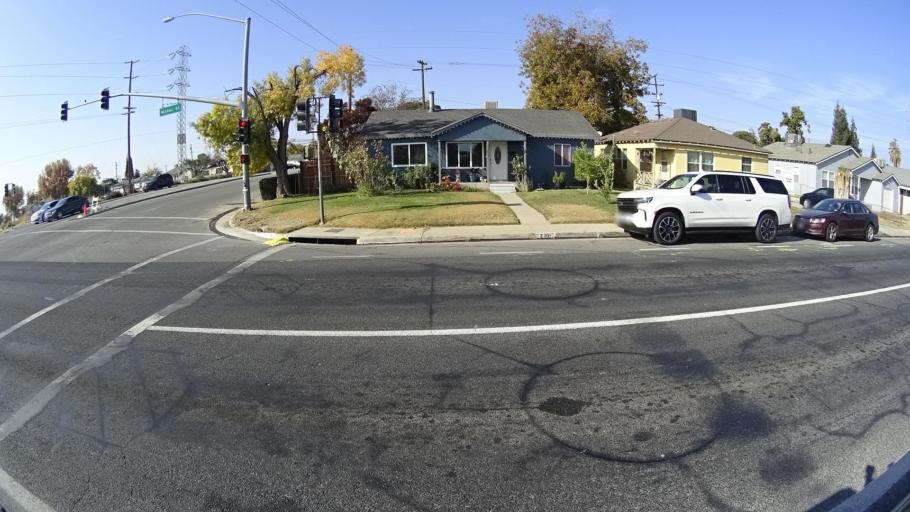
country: US
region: California
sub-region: Kern County
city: Oildale
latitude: 35.4270
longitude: -119.0124
